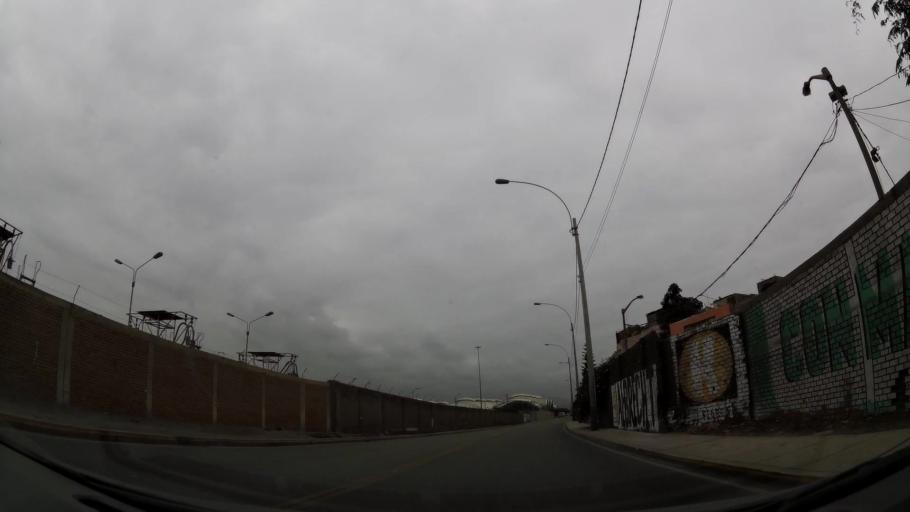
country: PE
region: Callao
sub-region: Callao
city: Callao
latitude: -12.0489
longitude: -77.1382
